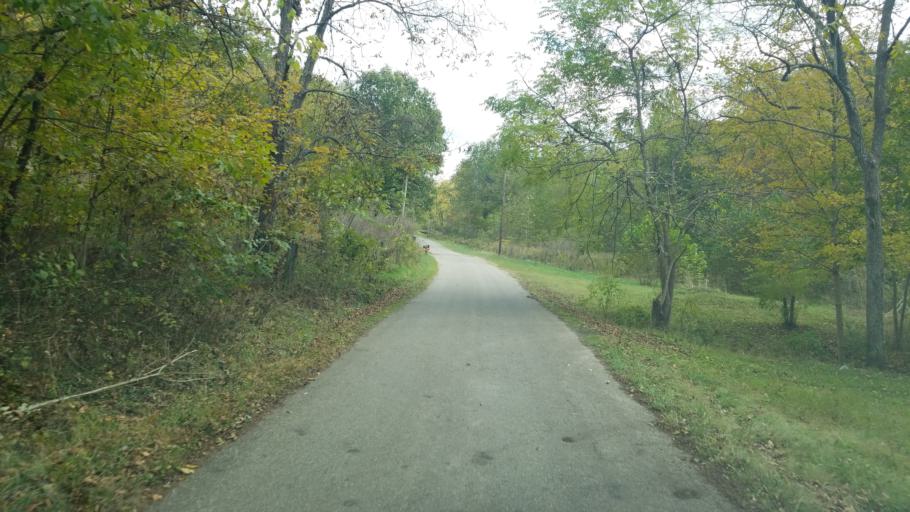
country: US
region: Ohio
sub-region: Jackson County
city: Jackson
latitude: 39.0934
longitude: -82.5943
